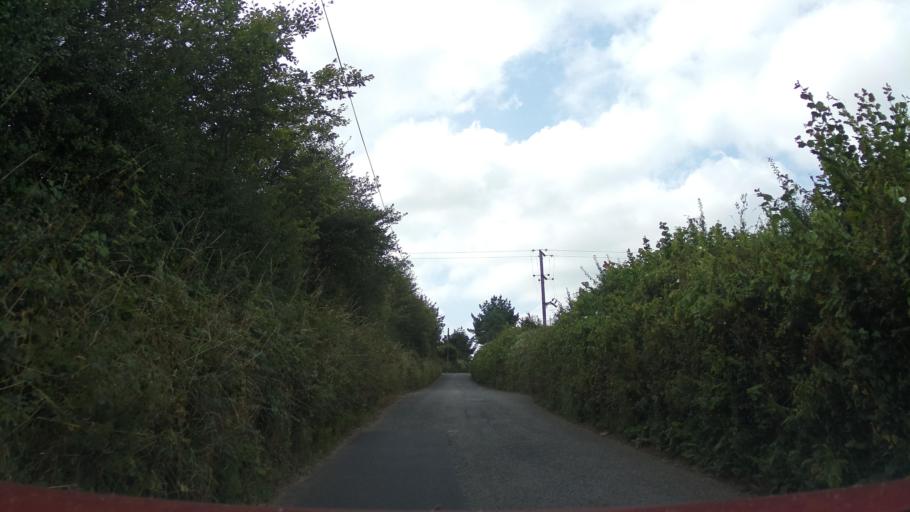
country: GB
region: England
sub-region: Devon
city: South Brent
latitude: 50.3999
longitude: -3.8317
